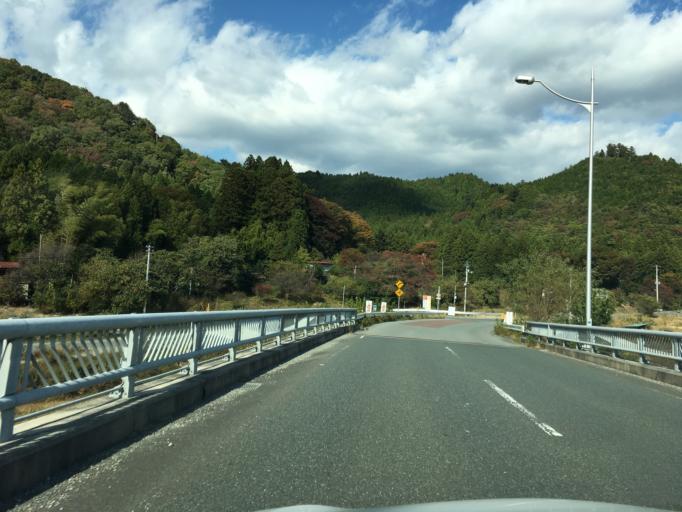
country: JP
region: Fukushima
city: Namie
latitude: 37.3657
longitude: 140.9519
